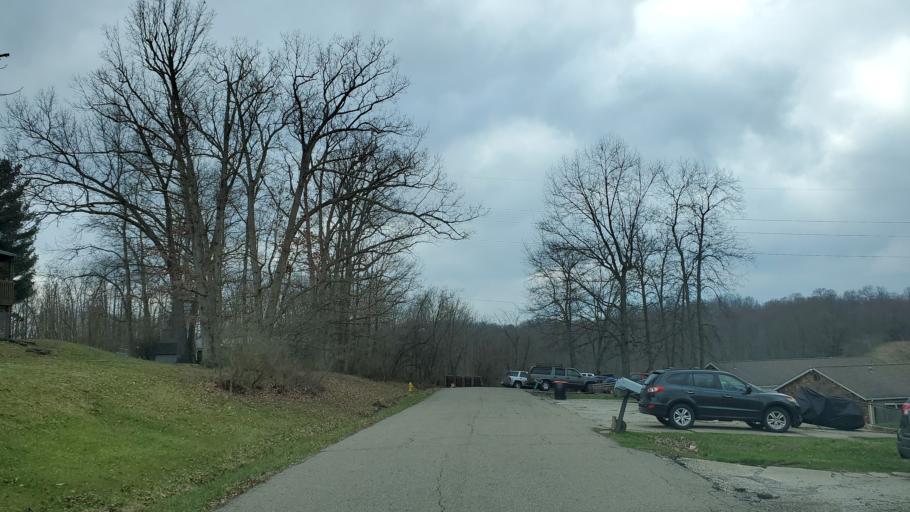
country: US
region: Ohio
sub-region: Licking County
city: Newark
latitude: 40.0275
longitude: -82.3820
